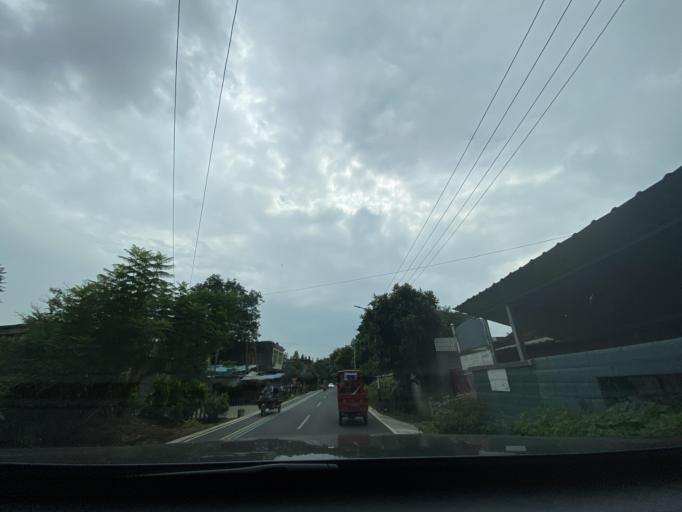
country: CN
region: Sichuan
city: Wujin
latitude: 30.4017
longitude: 103.9871
